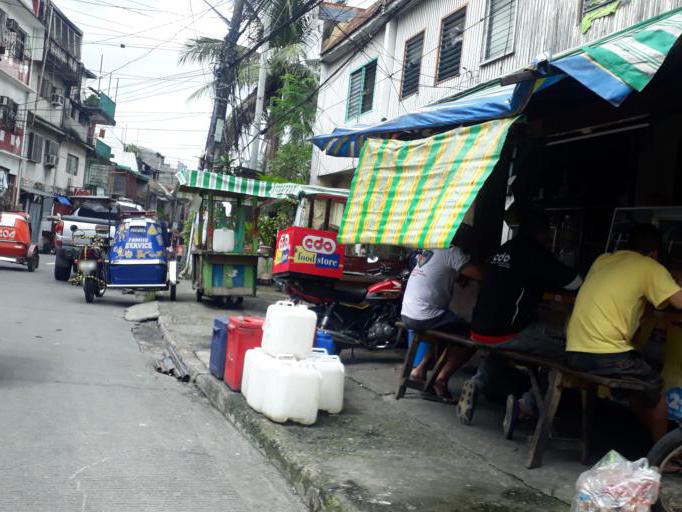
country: PH
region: Metro Manila
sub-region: San Juan
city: San Juan
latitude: 14.6176
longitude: 121.0488
